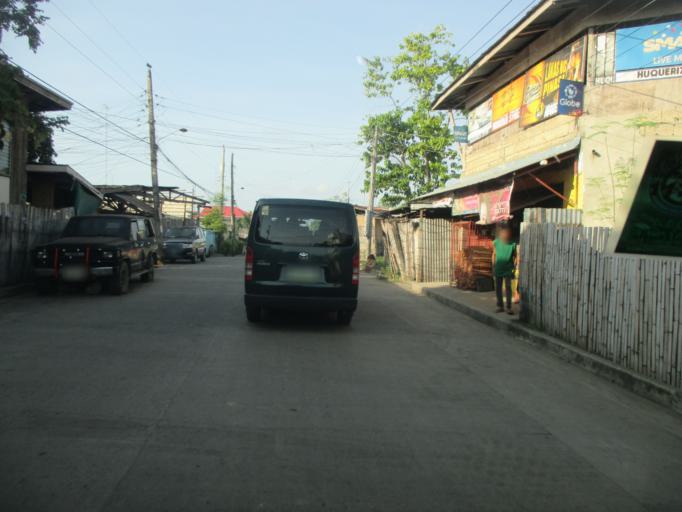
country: PH
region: Central Visayas
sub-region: Province of Bohol
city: Tagbilaran City
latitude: 9.6553
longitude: 123.8532
